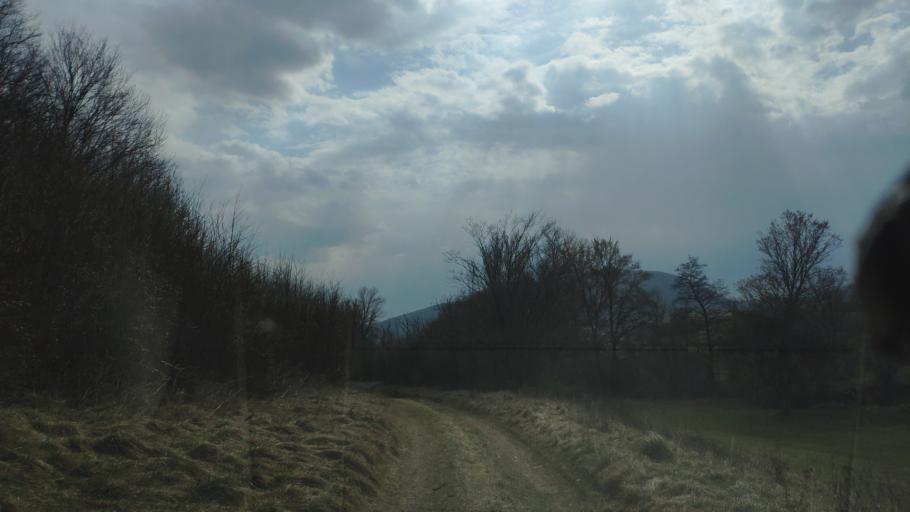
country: SK
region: Kosicky
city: Roznava
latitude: 48.6228
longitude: 20.3881
